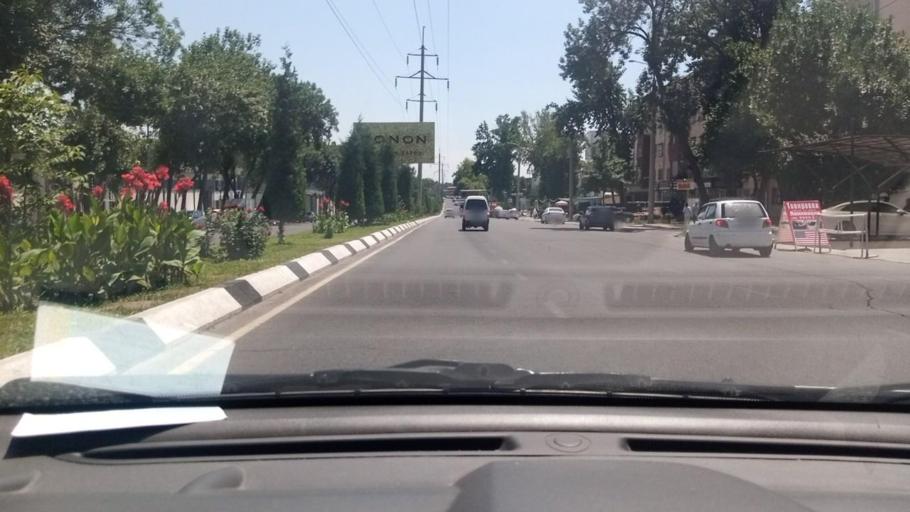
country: UZ
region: Toshkent Shahri
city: Tashkent
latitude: 41.2890
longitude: 69.1943
